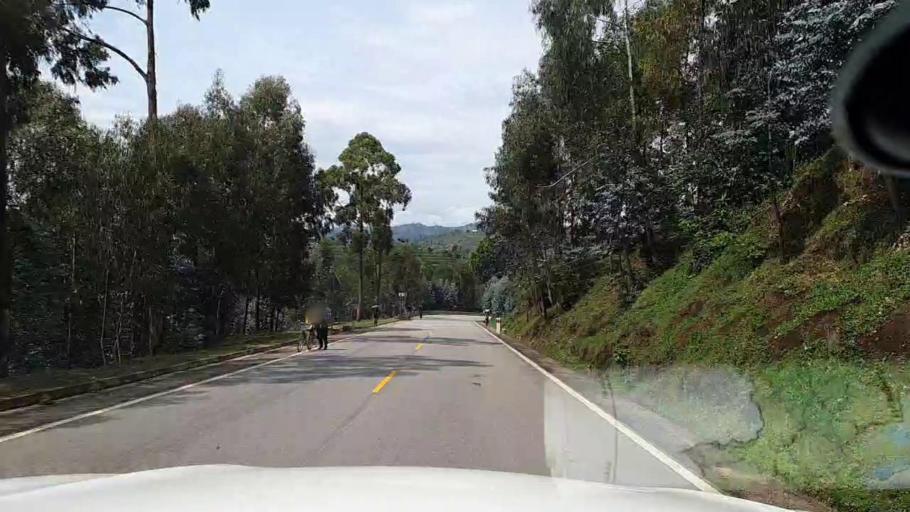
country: RW
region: Southern Province
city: Nzega
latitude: -2.5032
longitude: 29.5098
